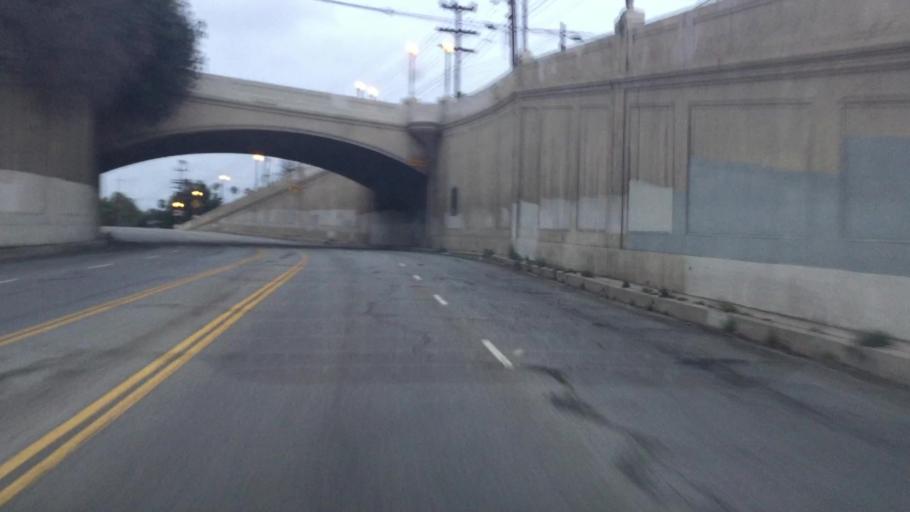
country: US
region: California
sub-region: Los Angeles County
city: Silver Lake
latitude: 34.1118
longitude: -118.2686
